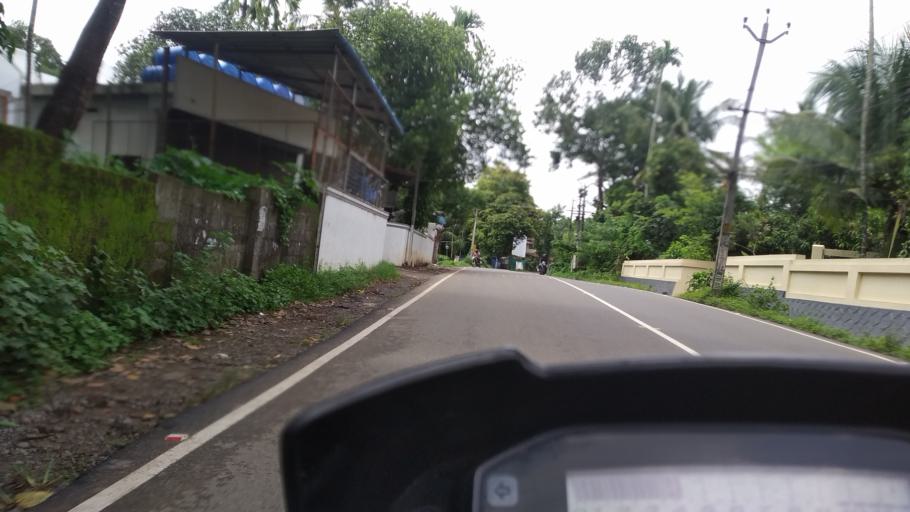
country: IN
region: Kerala
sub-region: Ernakulam
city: Aluva
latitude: 10.1293
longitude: 76.2965
